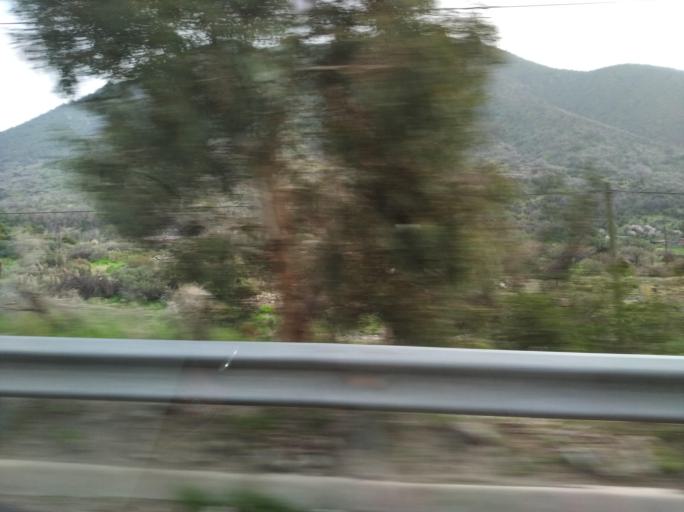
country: CL
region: Santiago Metropolitan
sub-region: Provincia de Chacabuco
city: Lampa
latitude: -33.0772
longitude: -70.9444
